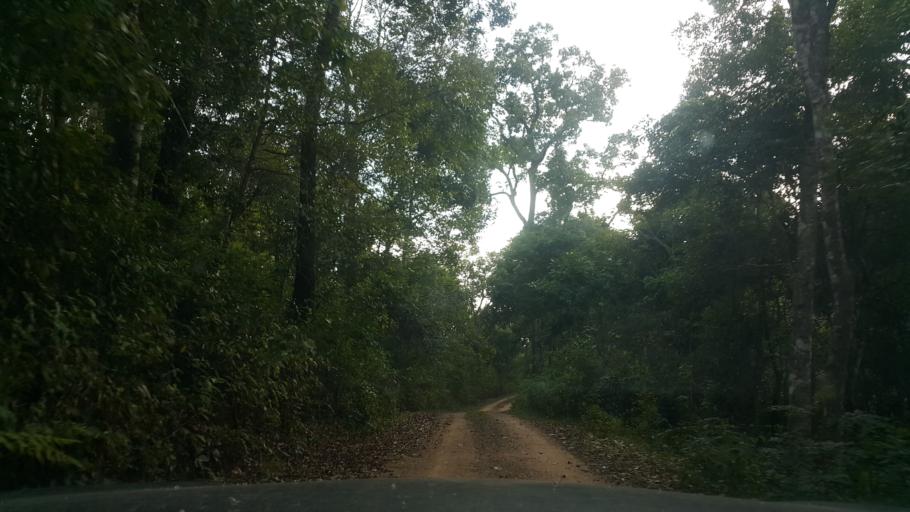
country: TH
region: Chiang Mai
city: Samoeng
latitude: 19.0322
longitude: 98.6500
